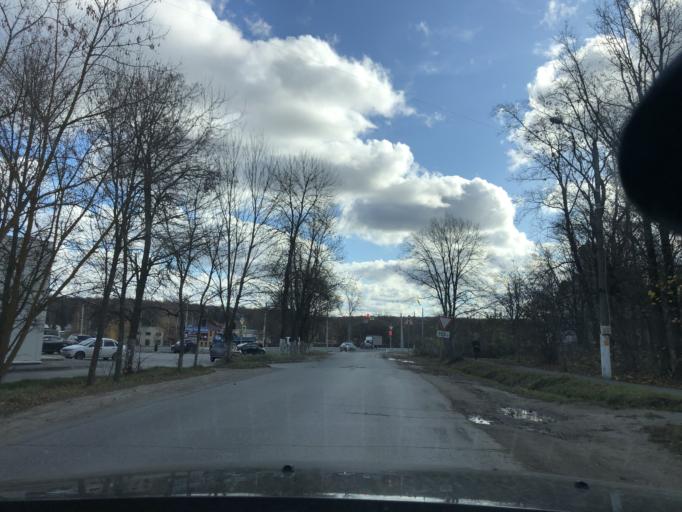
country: RU
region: Tula
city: Gorelki
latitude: 54.2950
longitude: 37.5770
